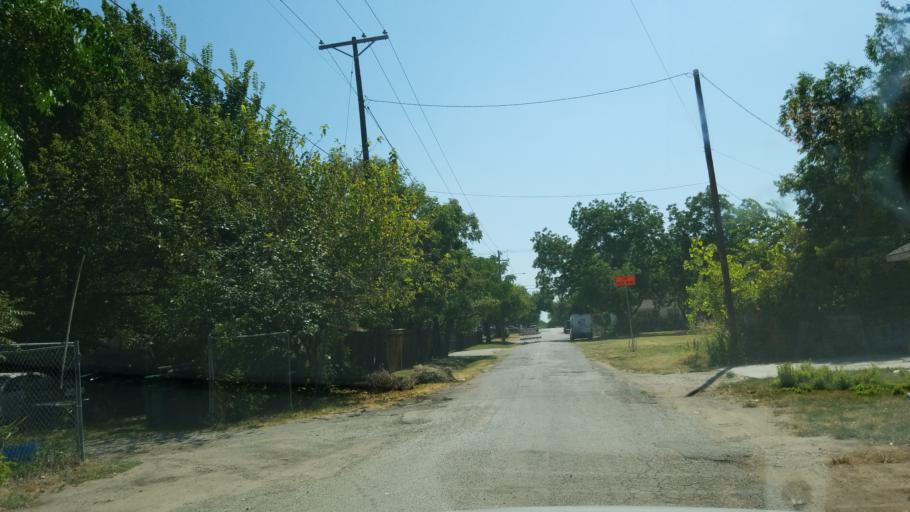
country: US
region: Texas
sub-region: Dallas County
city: Cockrell Hill
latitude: 32.7411
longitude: -96.8910
